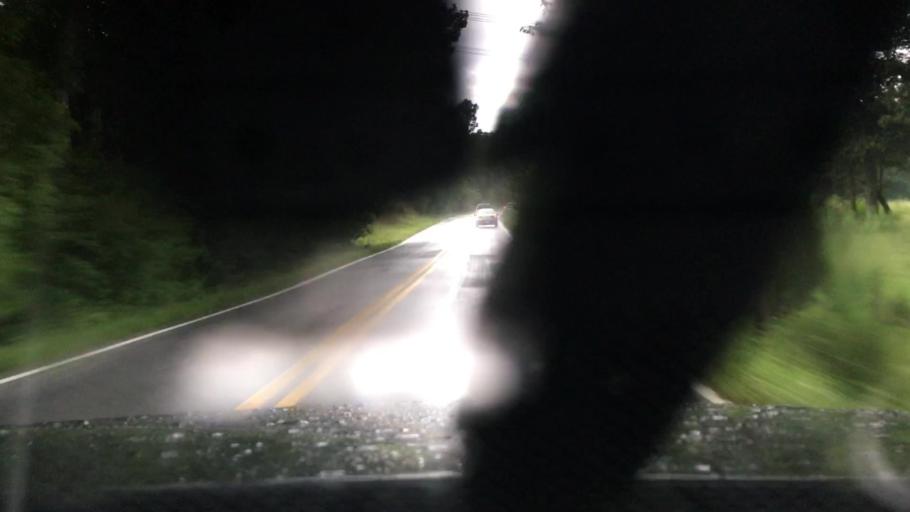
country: US
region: Virginia
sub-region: Campbell County
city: Timberlake
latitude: 37.2769
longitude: -79.2524
